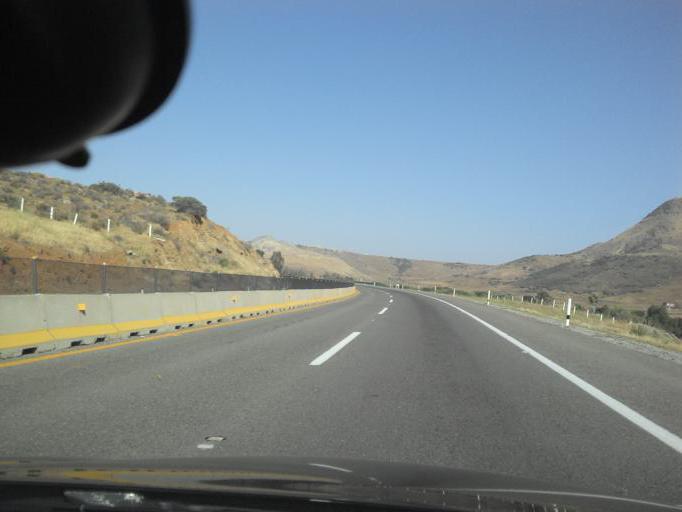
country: MX
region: Baja California
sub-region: Tijuana
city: El Nino
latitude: 32.5467
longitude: -116.7943
